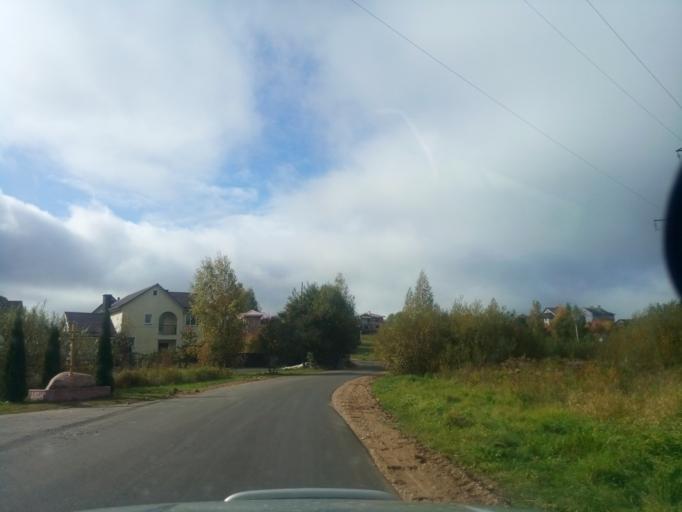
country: BY
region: Minsk
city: Zaslawye
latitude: 54.0019
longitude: 27.2701
